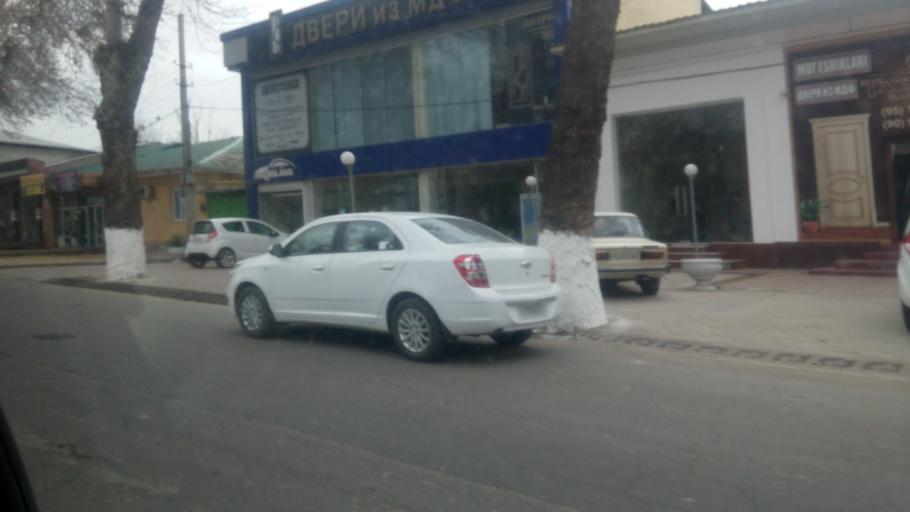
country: UZ
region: Toshkent Shahri
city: Tashkent
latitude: 41.3492
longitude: 69.2298
